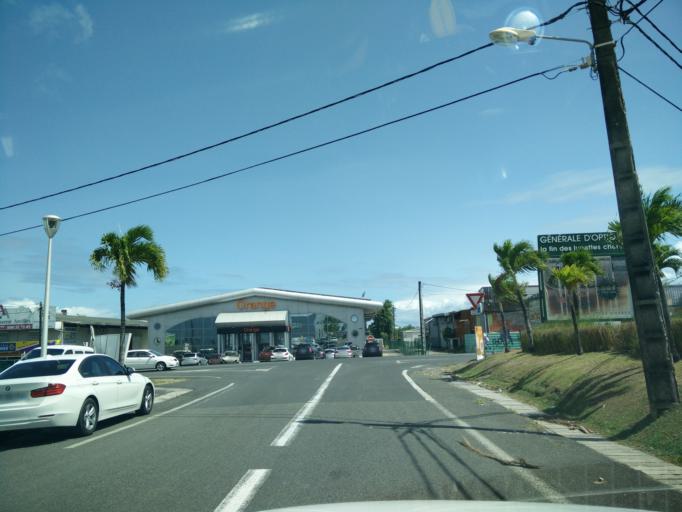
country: GP
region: Guadeloupe
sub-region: Guadeloupe
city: Pointe-a-Pitre
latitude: 16.2432
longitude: -61.5576
